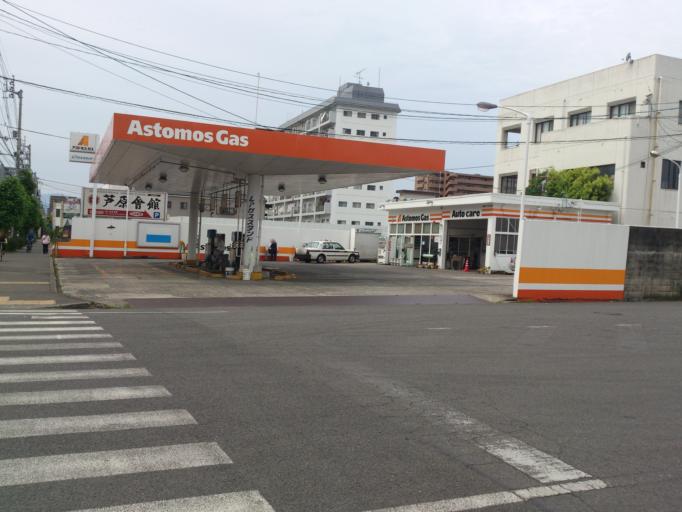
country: JP
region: Ehime
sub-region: Shikoku-chuo Shi
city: Matsuyama
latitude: 33.8389
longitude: 132.7524
